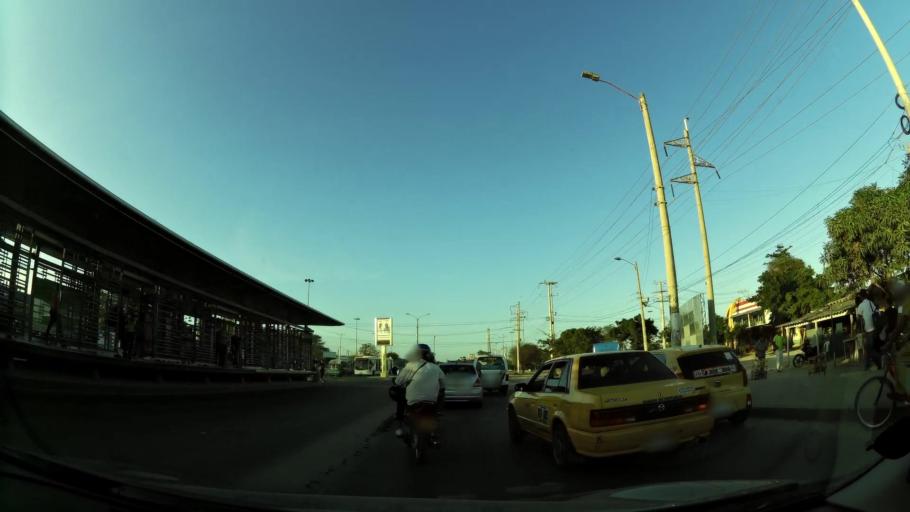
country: CO
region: Atlantico
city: Soledad
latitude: 10.9213
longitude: -74.7991
